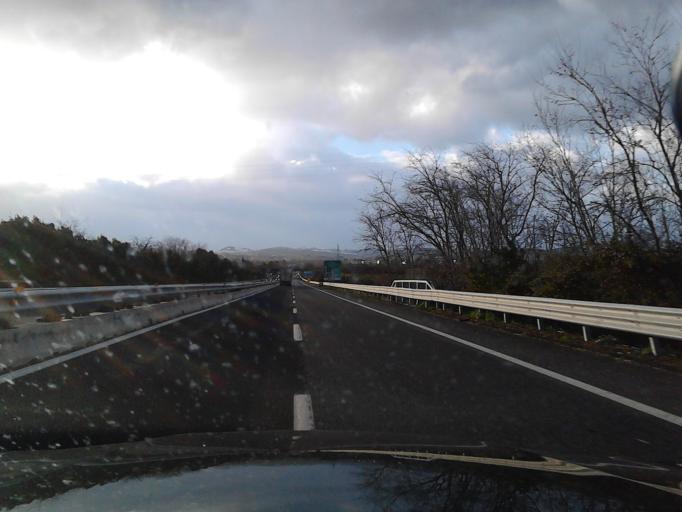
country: IT
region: Abruzzo
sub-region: Provincia di Chieti
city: Salvo Marina
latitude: 42.0571
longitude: 14.7823
